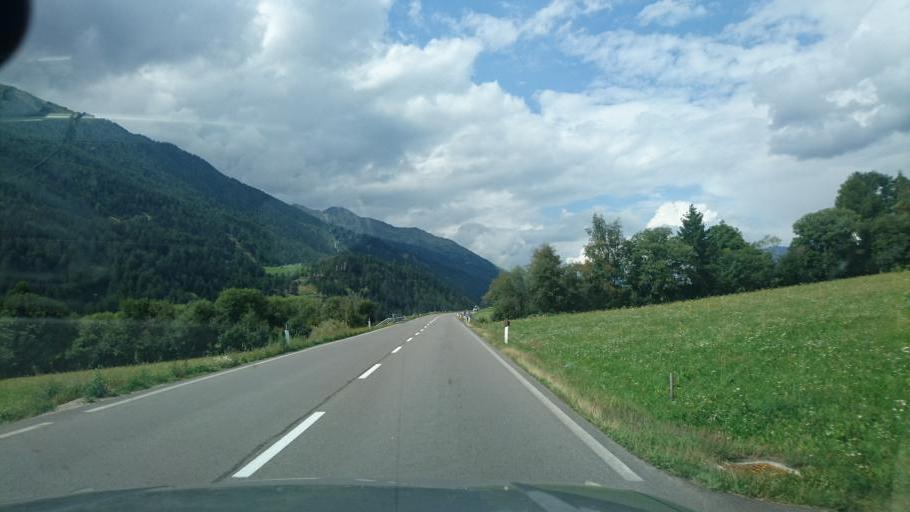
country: IT
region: Trentino-Alto Adige
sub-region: Bolzano
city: Malles Venosta
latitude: 46.7270
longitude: 10.5397
